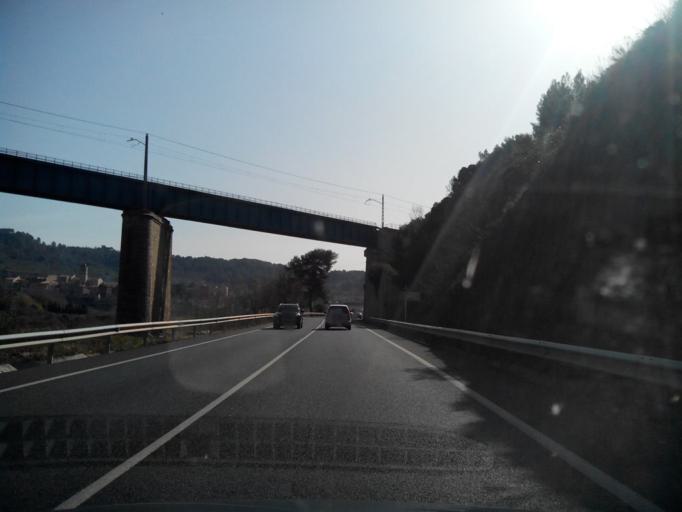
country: ES
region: Catalonia
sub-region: Provincia de Tarragona
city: Alcover
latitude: 41.3045
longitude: 1.1941
